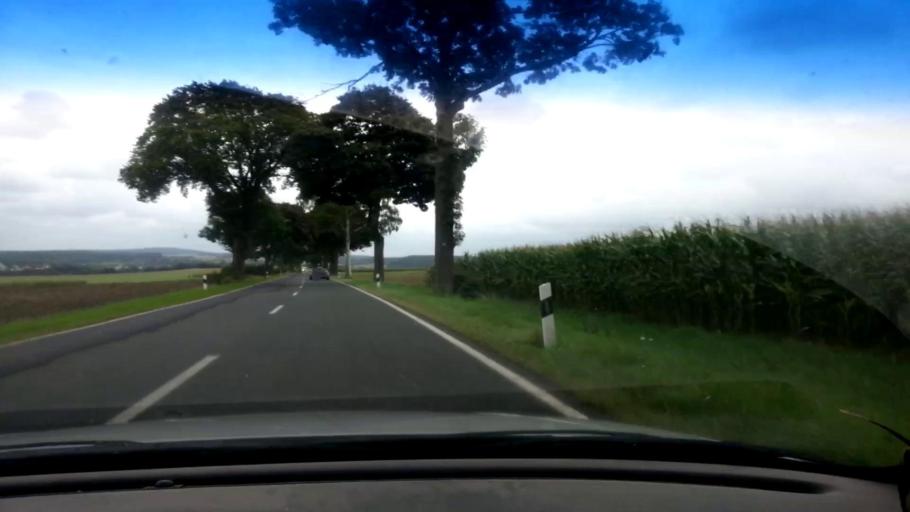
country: DE
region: Bavaria
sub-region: Upper Franconia
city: Grub
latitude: 50.0824
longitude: 11.9467
